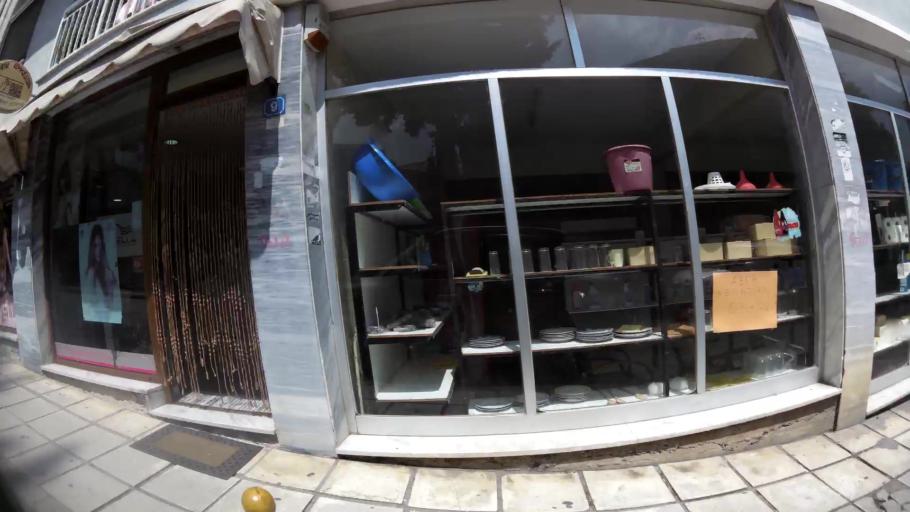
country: GR
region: Central Macedonia
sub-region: Nomos Imathias
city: Veroia
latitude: 40.5217
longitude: 22.2047
